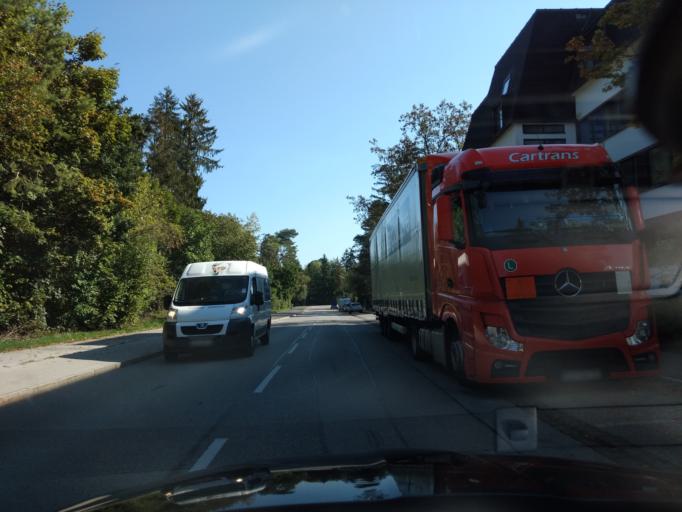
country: DE
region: Bavaria
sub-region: Upper Bavaria
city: Geretsried
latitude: 47.8814
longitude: 11.4701
